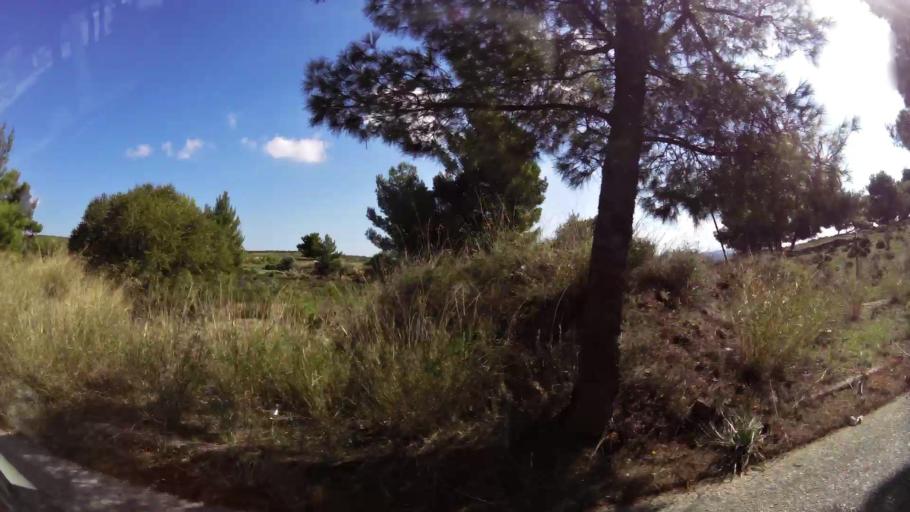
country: GR
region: Attica
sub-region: Nomarchia Anatolikis Attikis
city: Dioni
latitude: 38.0220
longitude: 23.9362
